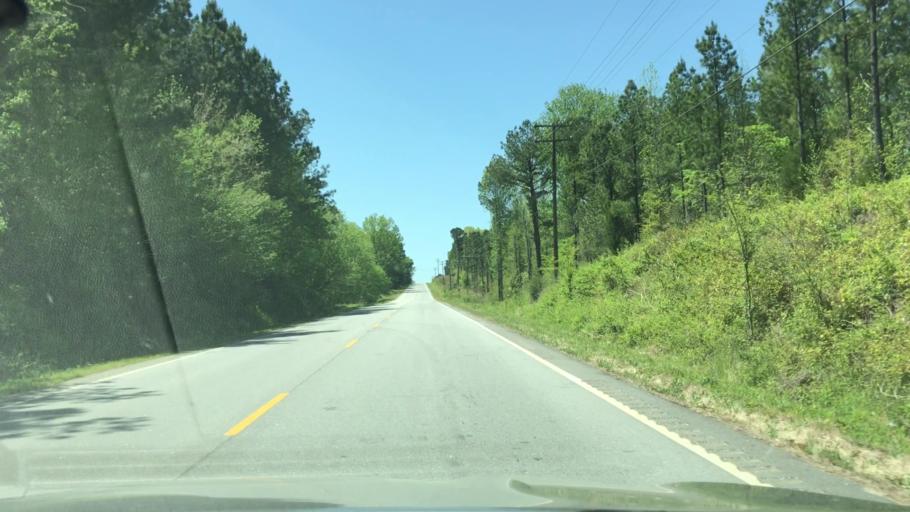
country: US
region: South Carolina
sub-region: Union County
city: Buffalo
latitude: 34.6831
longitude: -81.7096
